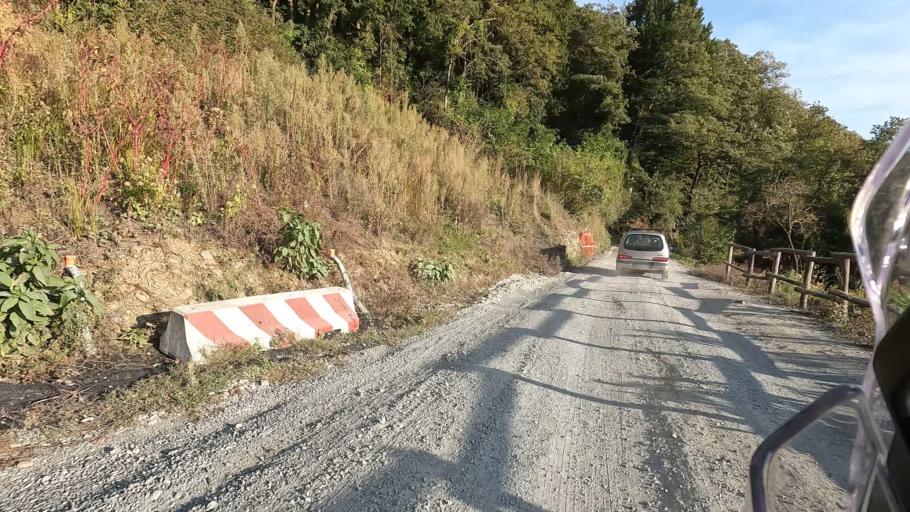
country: IT
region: Liguria
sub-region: Provincia di Savona
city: San Giovanni
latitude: 44.4092
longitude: 8.5219
